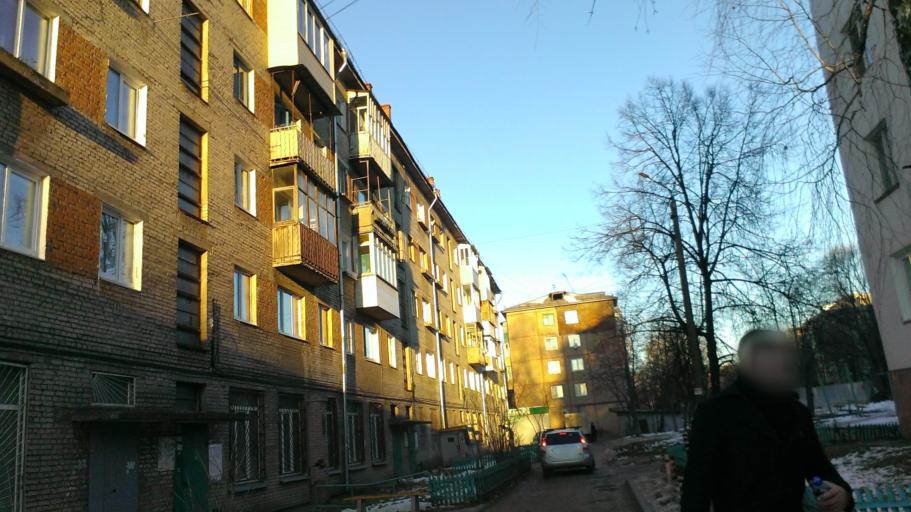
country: RU
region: Tula
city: Tula
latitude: 54.1933
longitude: 37.6863
